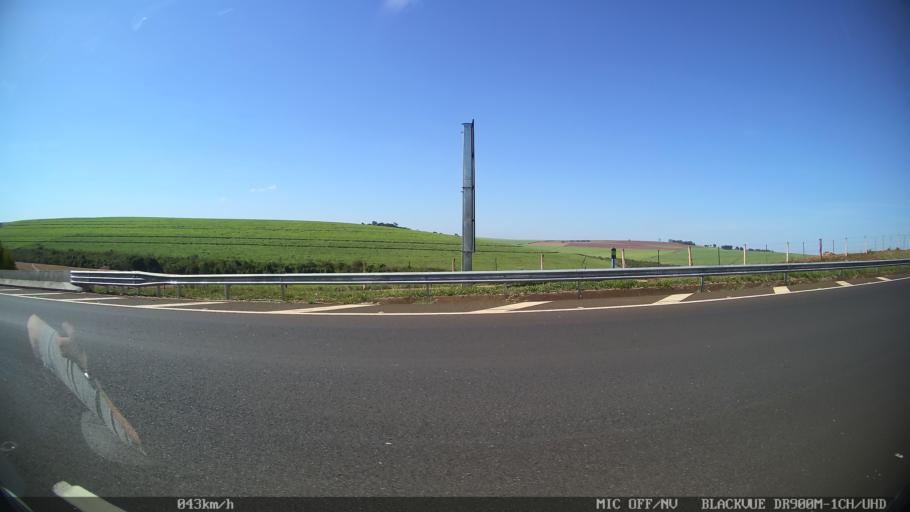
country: BR
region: Sao Paulo
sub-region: Batatais
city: Batatais
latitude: -20.7119
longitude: -47.5054
